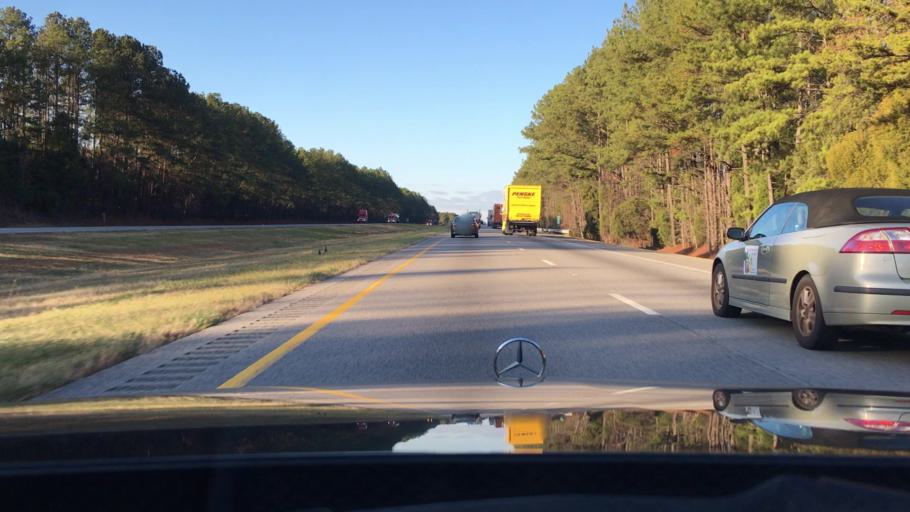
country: US
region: South Carolina
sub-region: Chester County
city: Eureka Mill
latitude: 34.7351
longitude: -81.0344
